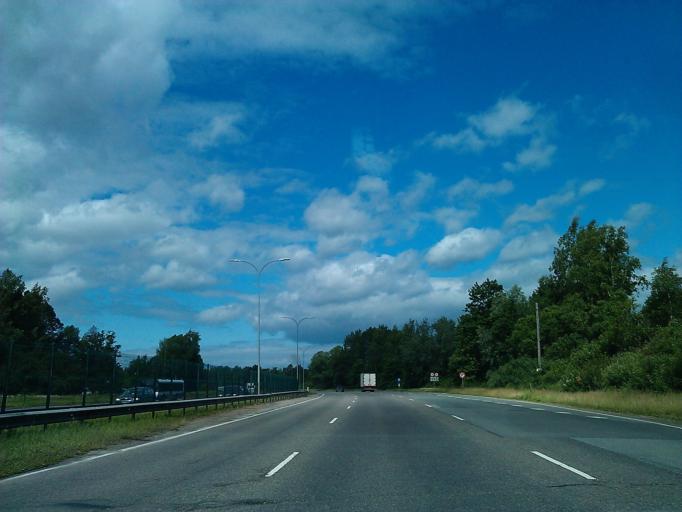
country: LV
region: Marupe
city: Marupe
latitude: 56.9475
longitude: 23.9910
